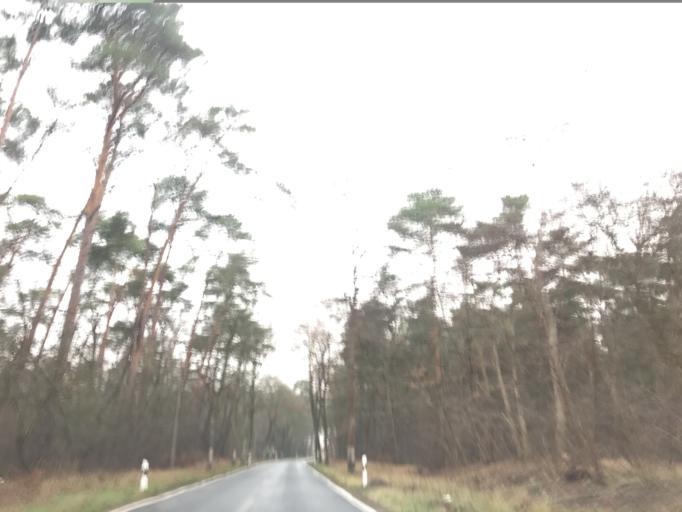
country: DE
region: Brandenburg
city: Brieselang
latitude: 52.6629
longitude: 12.9809
